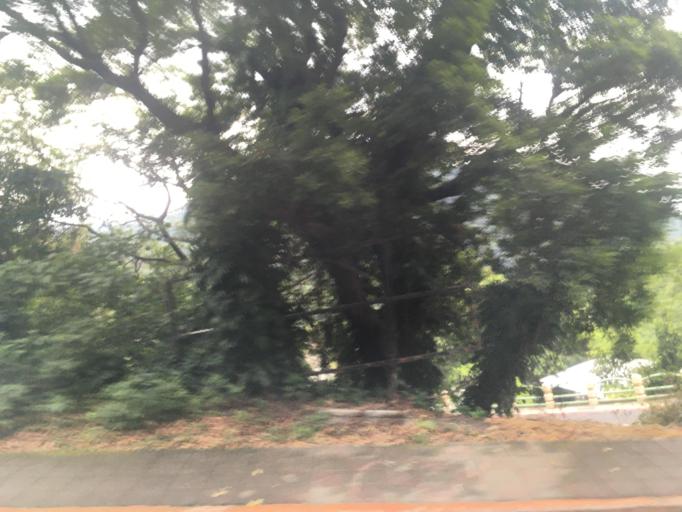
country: TW
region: Taipei
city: Taipei
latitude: 25.1410
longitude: 121.5279
